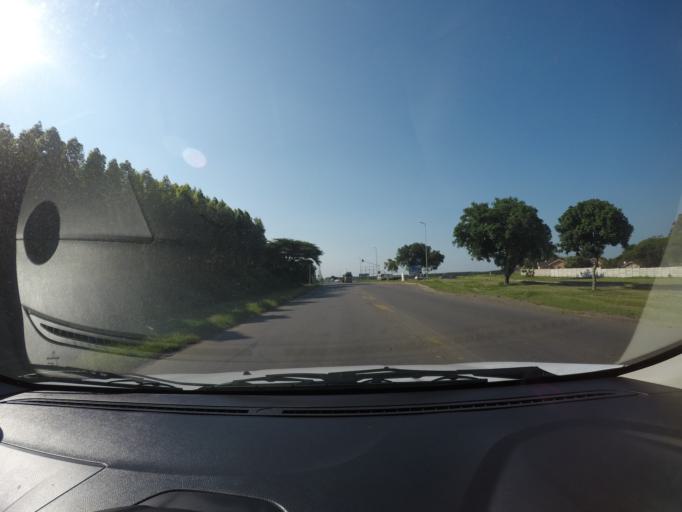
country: ZA
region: KwaZulu-Natal
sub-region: uThungulu District Municipality
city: Richards Bay
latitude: -28.7163
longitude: 32.0312
